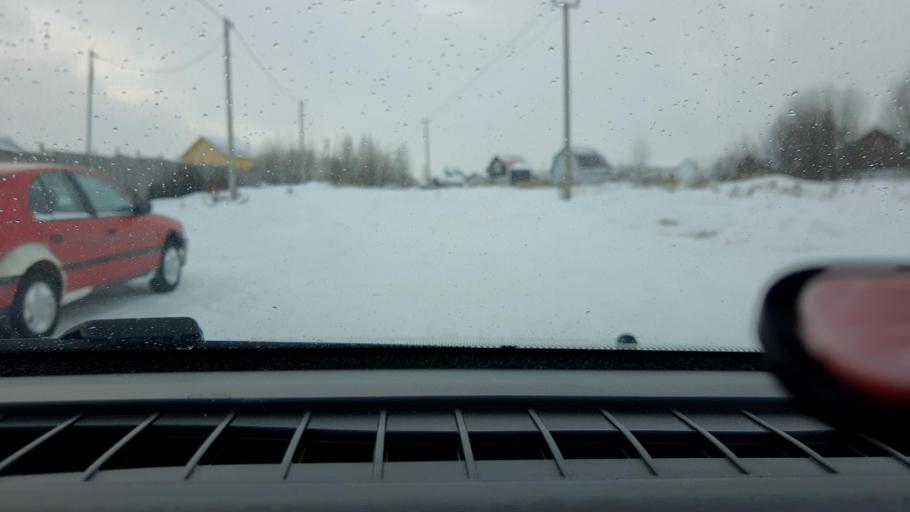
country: RU
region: Nizjnij Novgorod
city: Burevestnik
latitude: 56.1497
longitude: 43.7418
